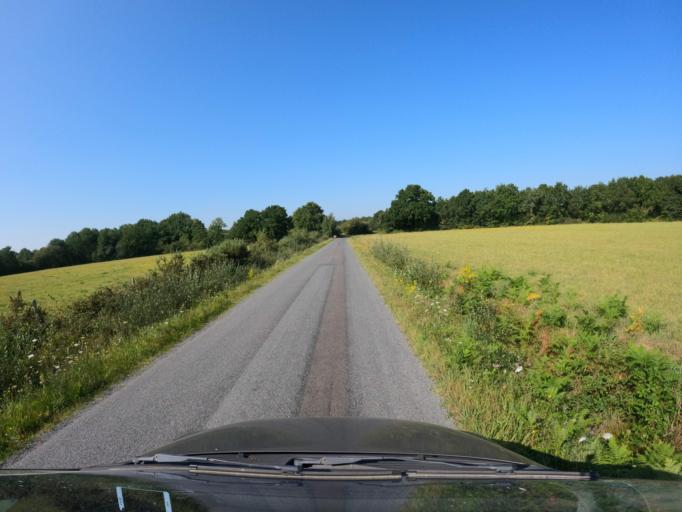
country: FR
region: Pays de la Loire
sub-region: Departement de la Loire-Atlantique
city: Geneston
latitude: 47.0637
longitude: -1.5337
